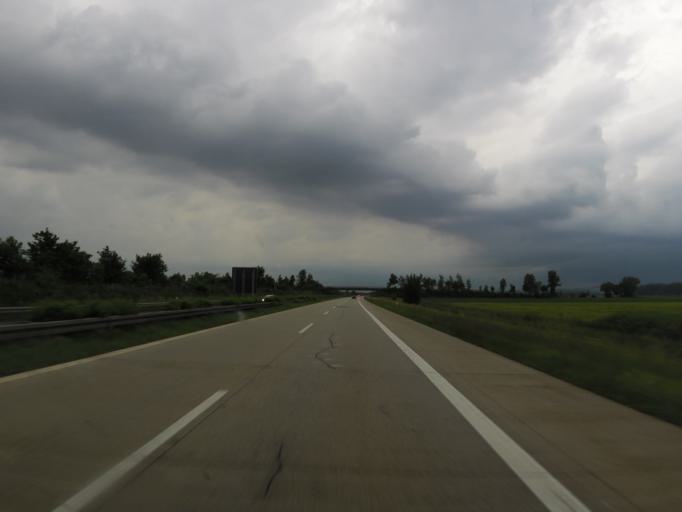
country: DE
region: Bavaria
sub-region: Lower Bavaria
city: Loiching
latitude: 48.6449
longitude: 12.4259
